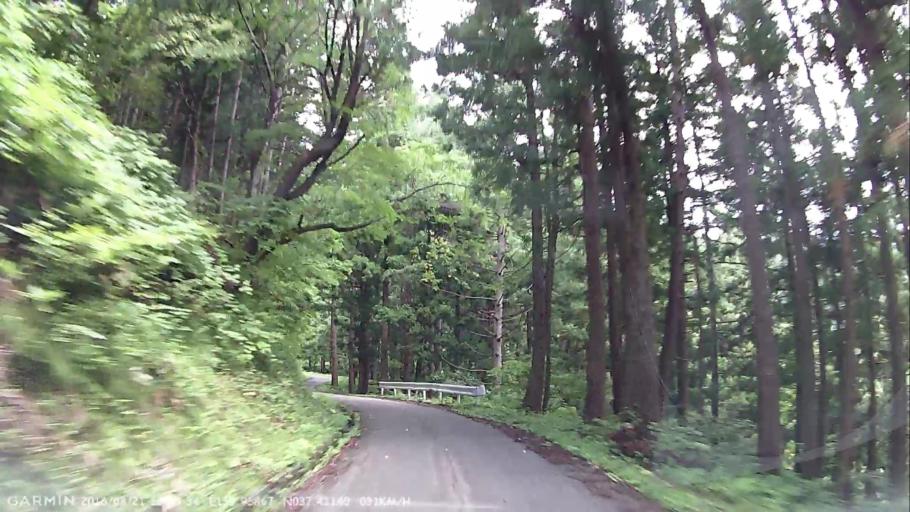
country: JP
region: Fukushima
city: Inawashiro
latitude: 37.4114
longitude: 139.9587
